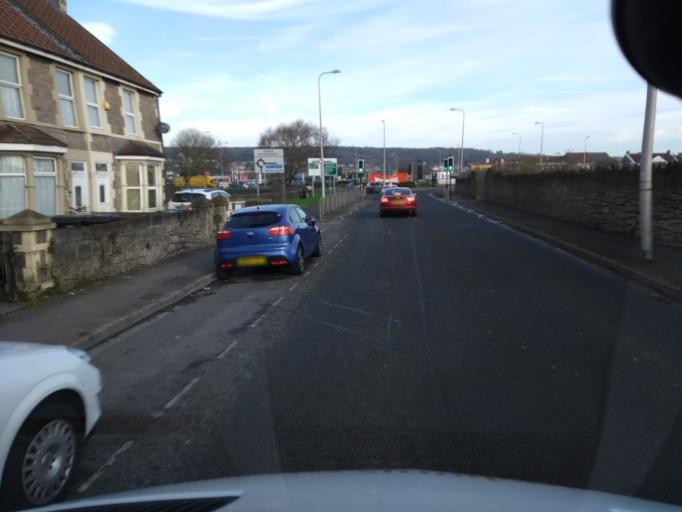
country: GB
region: England
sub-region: North Somerset
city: Weston-super-Mare
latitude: 51.3422
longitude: -2.9681
